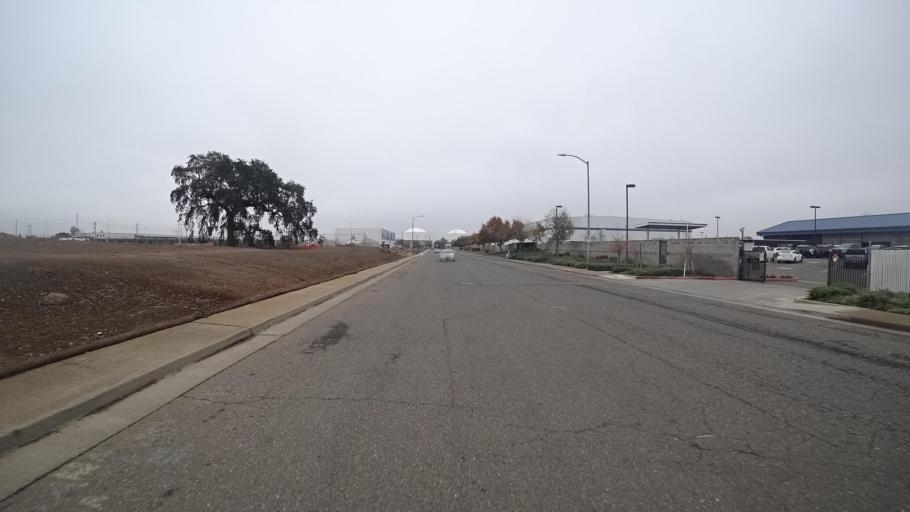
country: US
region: California
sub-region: Sacramento County
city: Elk Grove
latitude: 38.3876
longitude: -121.3595
